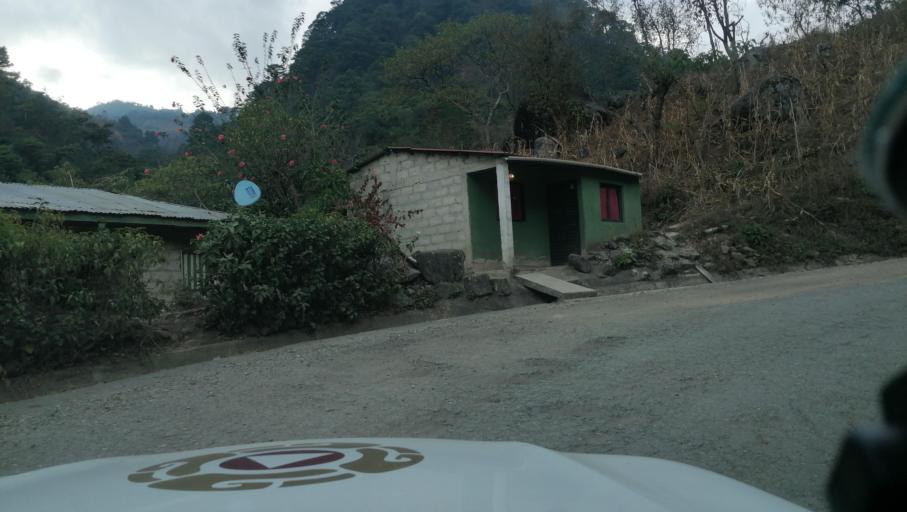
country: GT
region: San Marcos
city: Tacana
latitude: 15.2115
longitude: -92.1997
